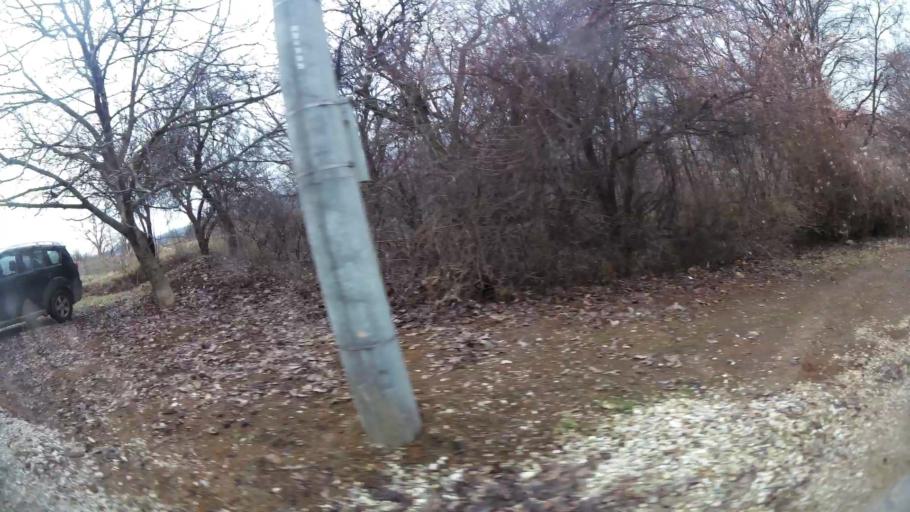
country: BG
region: Sofia-Capital
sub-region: Stolichna Obshtina
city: Sofia
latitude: 42.6150
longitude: 23.3564
